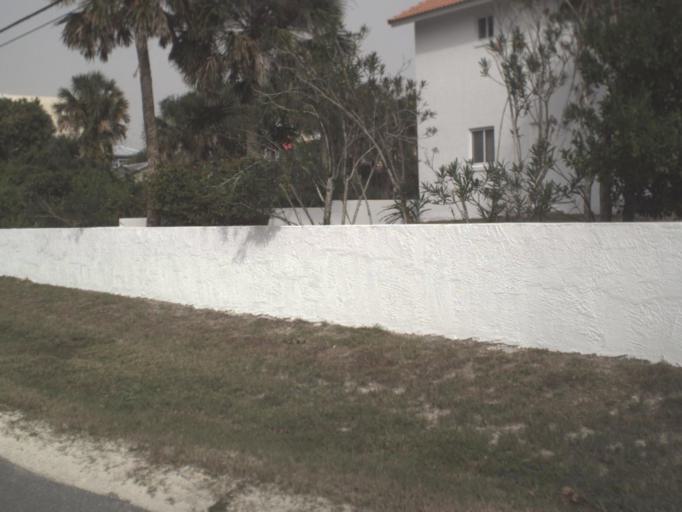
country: US
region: Florida
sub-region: Volusia County
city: Edgewater
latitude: 29.0235
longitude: -80.8881
